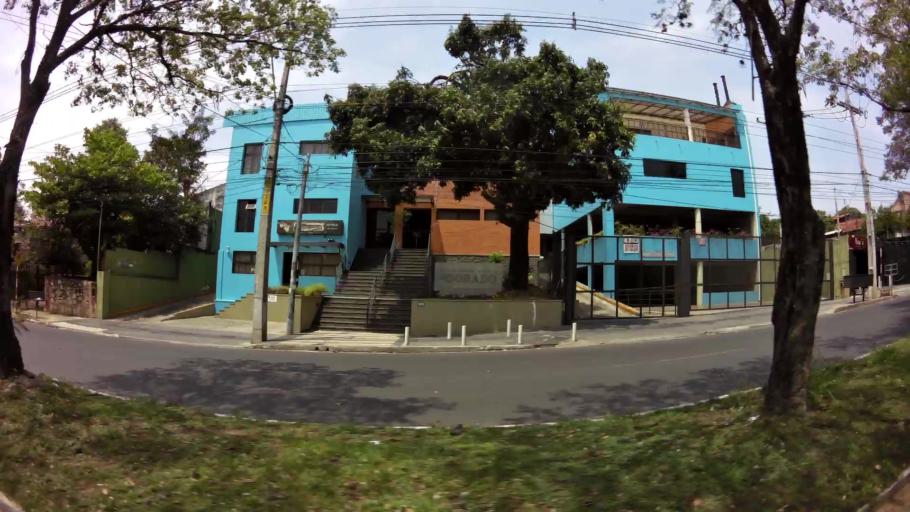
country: PY
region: Asuncion
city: Asuncion
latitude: -25.2801
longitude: -57.6003
